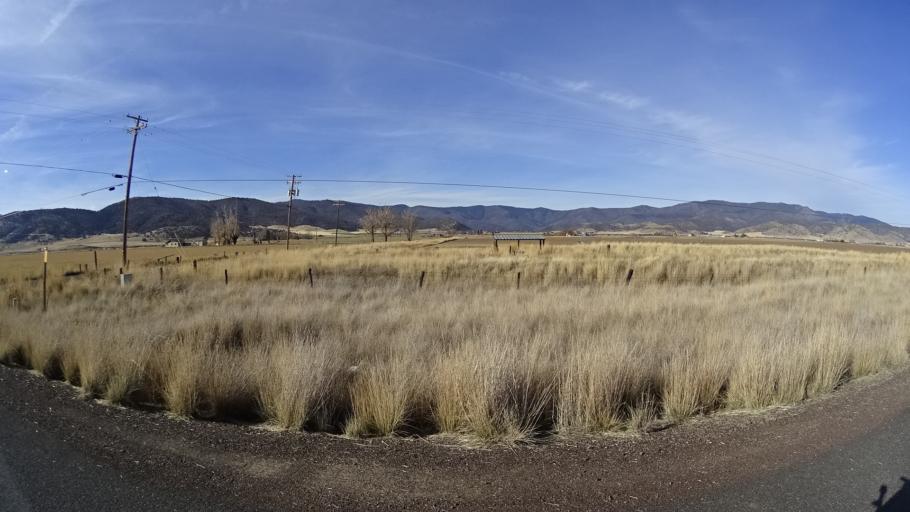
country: US
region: California
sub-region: Siskiyou County
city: Weed
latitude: 41.5384
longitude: -122.5253
